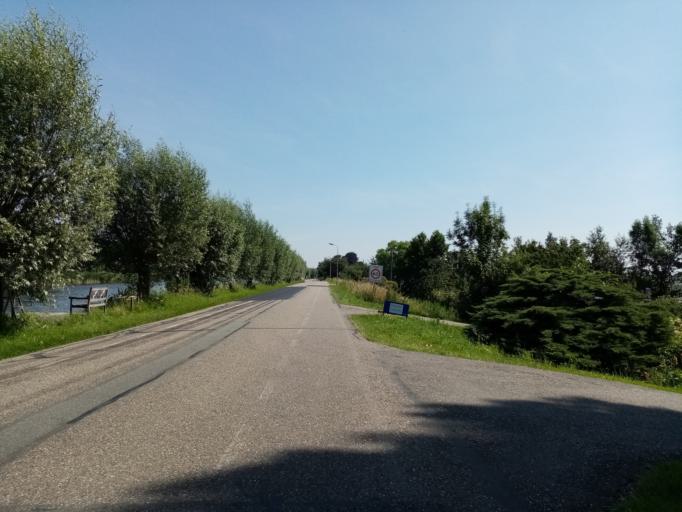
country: NL
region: North Holland
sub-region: Gemeente Aalsmeer
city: Aalsmeer
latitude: 52.2184
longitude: 4.7635
